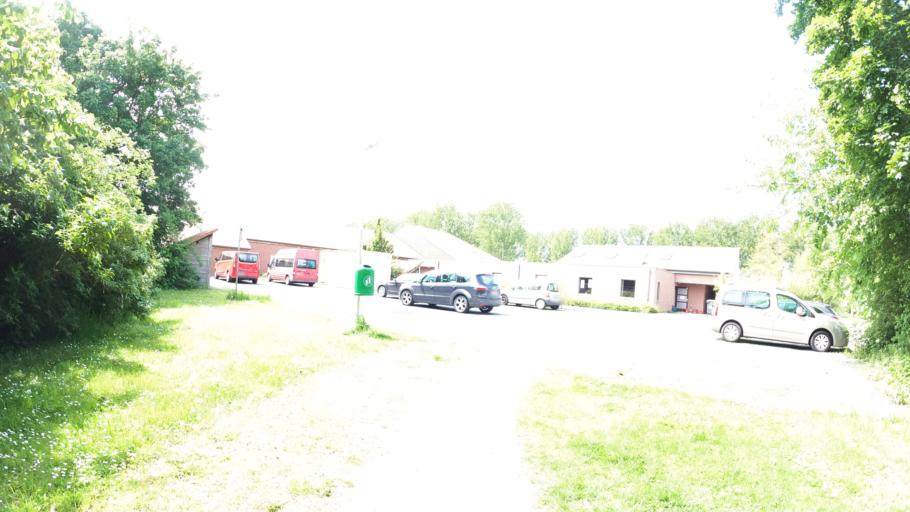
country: BE
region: Flanders
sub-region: Provincie Oost-Vlaanderen
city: Beveren
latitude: 51.2506
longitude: 4.2728
